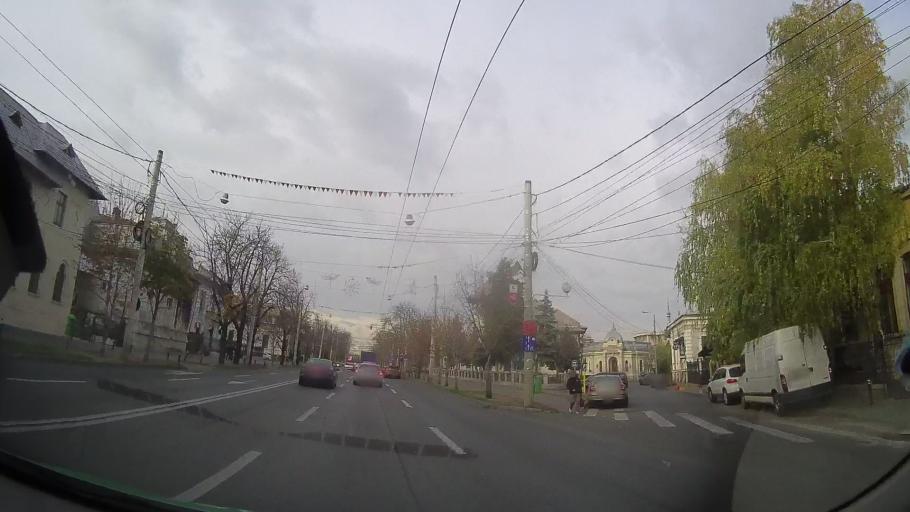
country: RO
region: Prahova
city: Ploiesti
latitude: 44.9353
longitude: 26.0264
